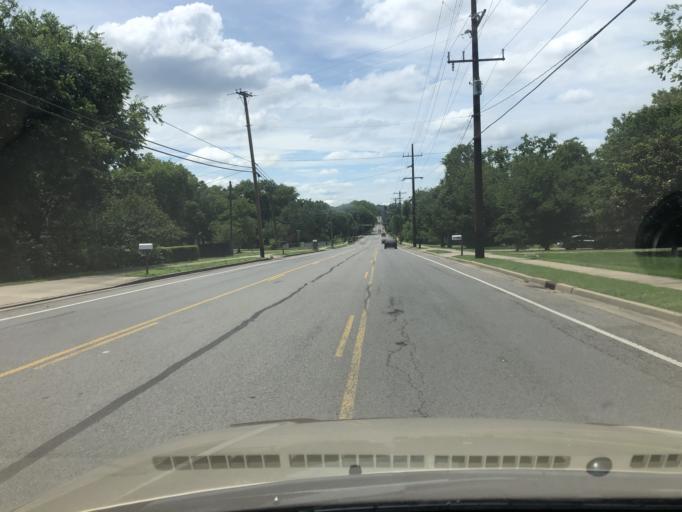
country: US
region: Tennessee
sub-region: Davidson County
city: Goodlettsville
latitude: 36.2555
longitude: -86.7046
